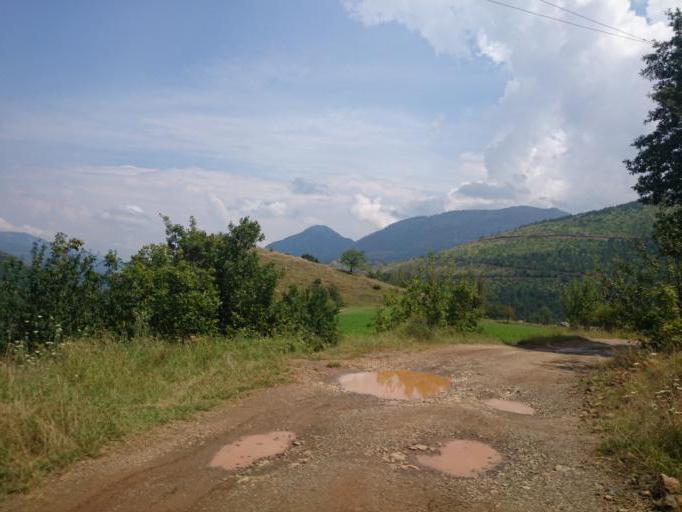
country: AL
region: Diber
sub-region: Rrethi i Dibres
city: Fushe-Lure
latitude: 41.8328
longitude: 20.1855
